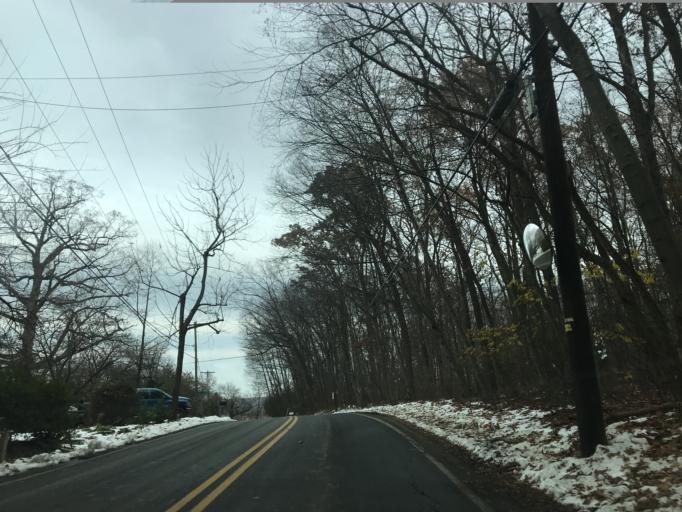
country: US
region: Pennsylvania
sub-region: York County
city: Susquehanna Trails
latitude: 39.6924
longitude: -76.4084
